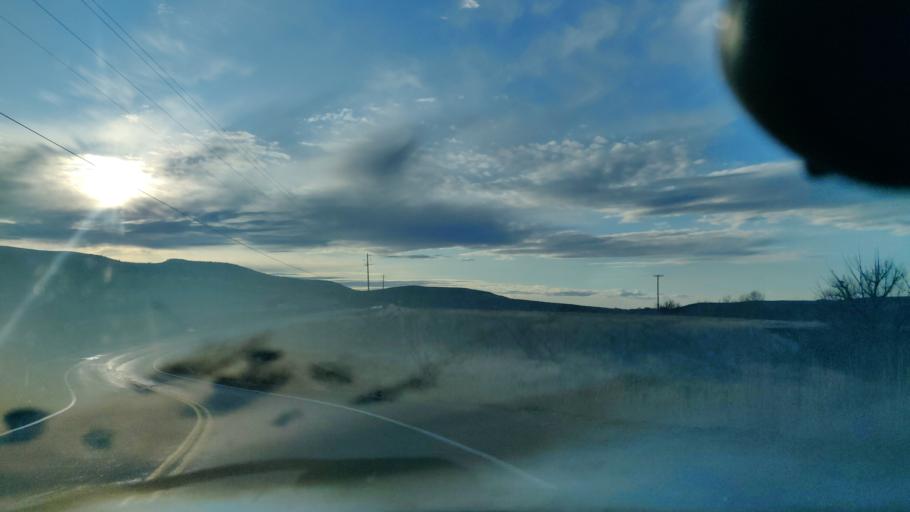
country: US
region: Idaho
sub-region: Ada County
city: Eagle
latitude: 43.7307
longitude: -116.2763
